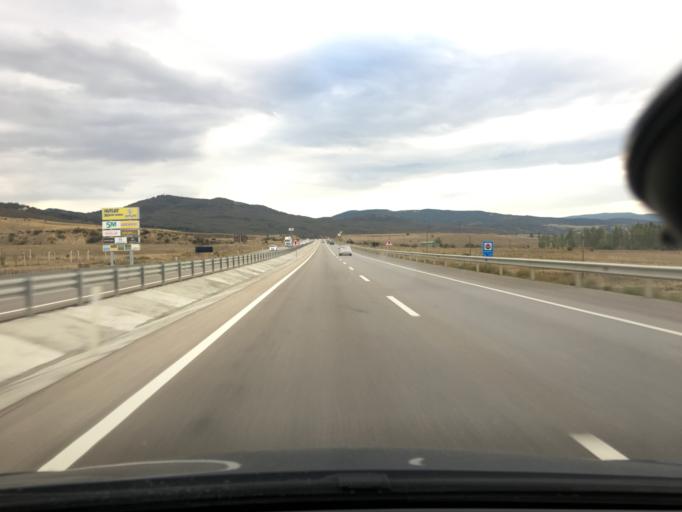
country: TR
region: Afyonkarahisar
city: Sincanli
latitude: 38.7191
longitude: 30.3320
